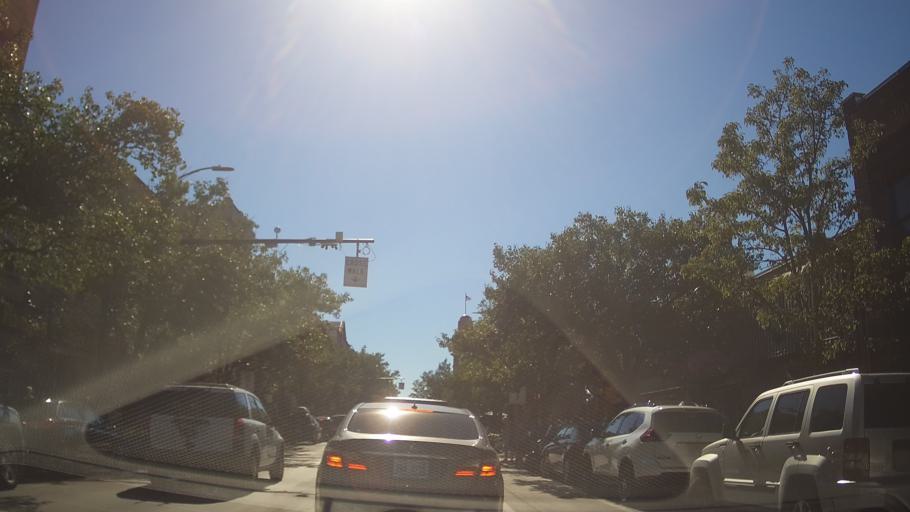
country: US
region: Michigan
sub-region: Grand Traverse County
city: Traverse City
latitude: 44.7641
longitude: -85.6216
